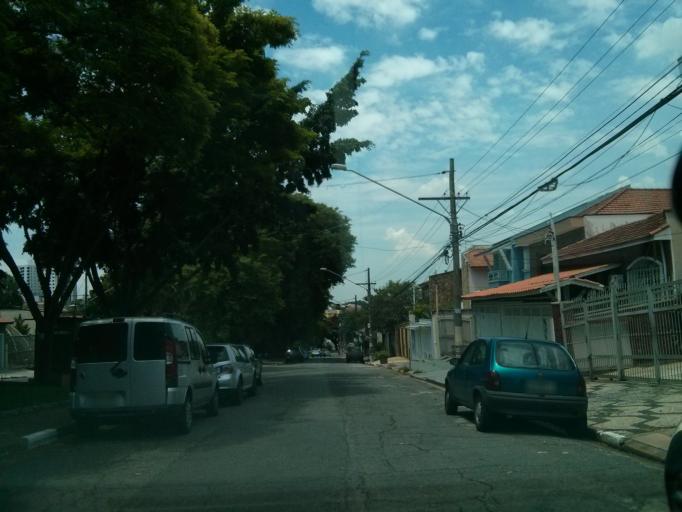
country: BR
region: Sao Paulo
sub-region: Sao Caetano Do Sul
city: Sao Caetano do Sul
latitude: -23.6154
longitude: -46.6138
